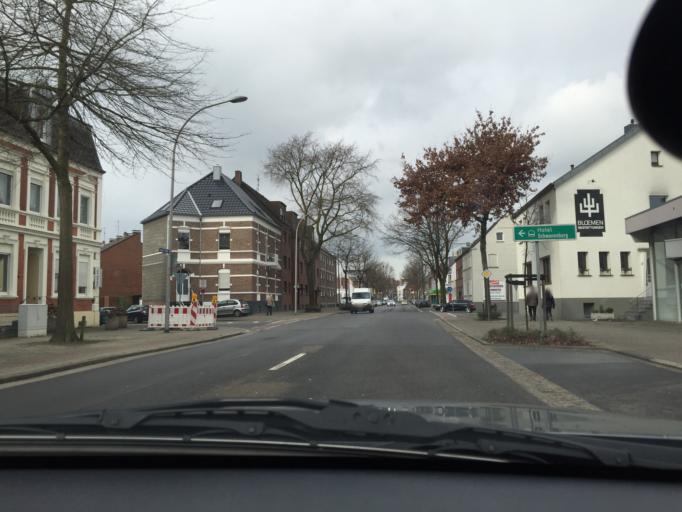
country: DE
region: North Rhine-Westphalia
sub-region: Regierungsbezirk Dusseldorf
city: Kleve
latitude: 51.7858
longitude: 6.1468
